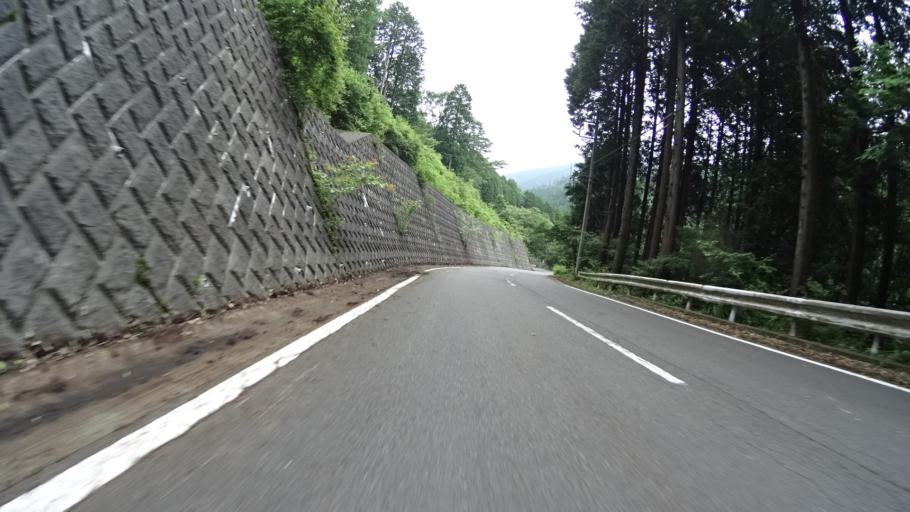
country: JP
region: Kanagawa
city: Hadano
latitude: 35.4323
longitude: 139.2103
